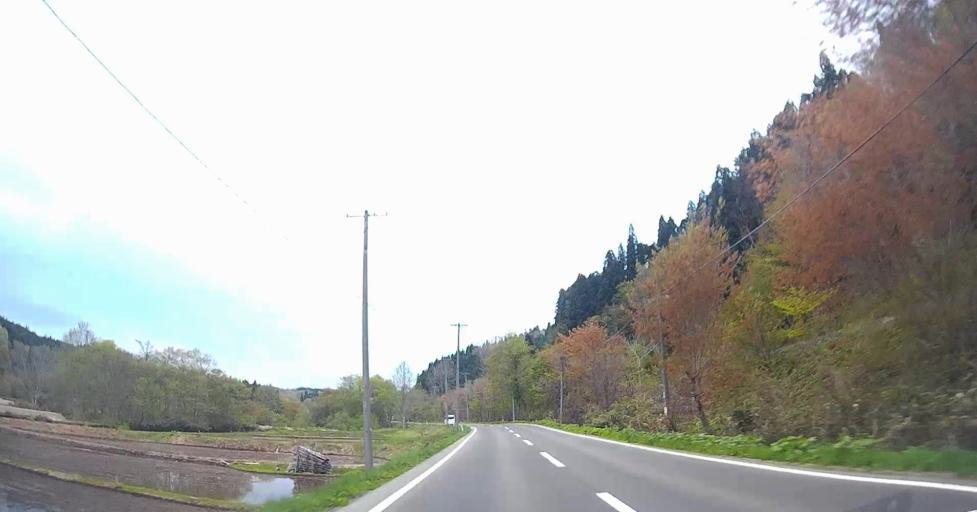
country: JP
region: Aomori
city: Goshogawara
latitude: 41.1247
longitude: 140.5198
